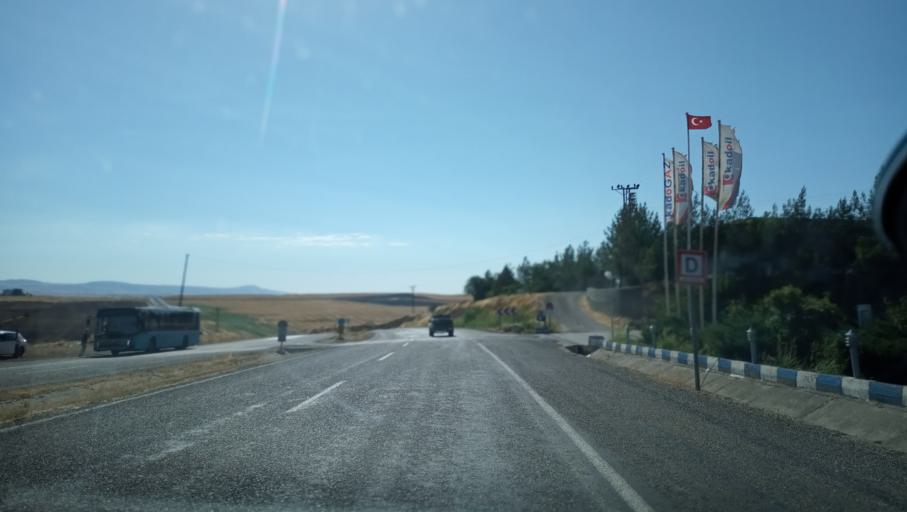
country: TR
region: Diyarbakir
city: Bagdere
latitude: 38.1282
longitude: 40.7791
